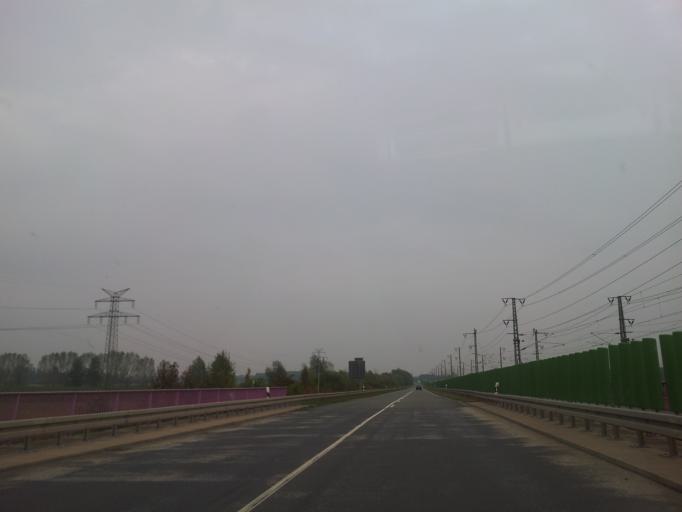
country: DE
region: Saxony-Anhalt
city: Stendal
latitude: 52.5761
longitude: 11.8753
